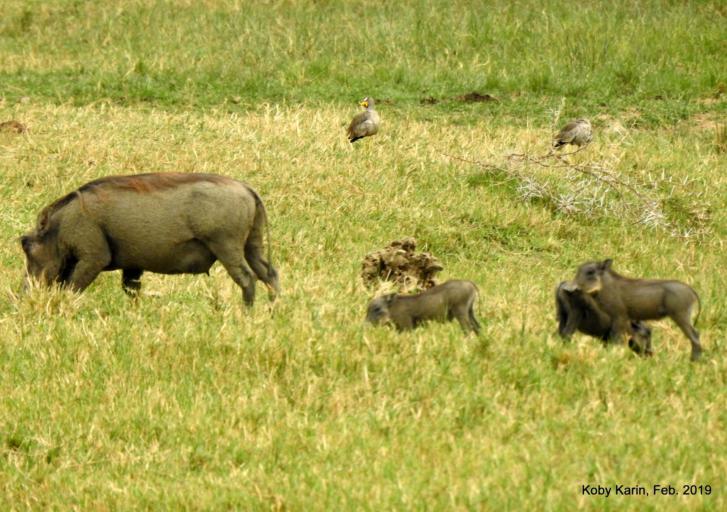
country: UG
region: Western Region
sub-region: Rubirizi District
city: Rubirizi
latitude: -0.1981
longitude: 29.9090
